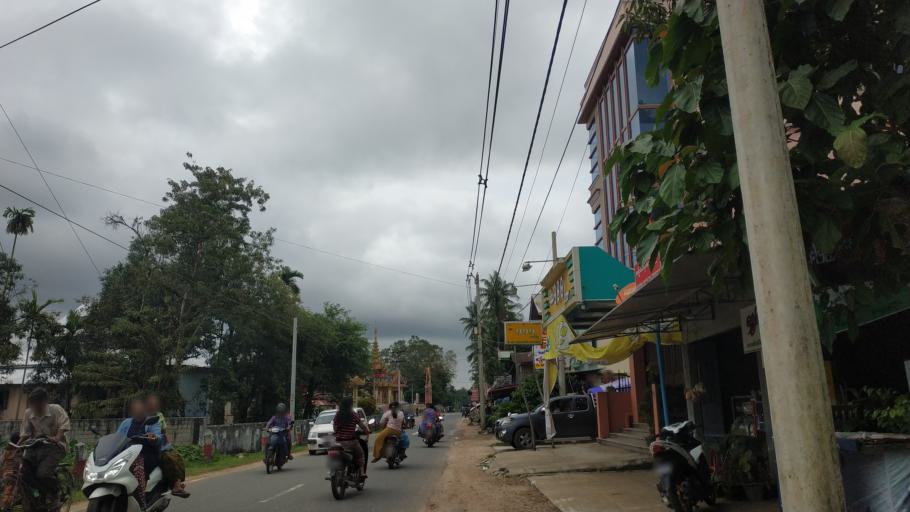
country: MM
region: Tanintharyi
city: Dawei
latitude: 14.0782
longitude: 98.1975
